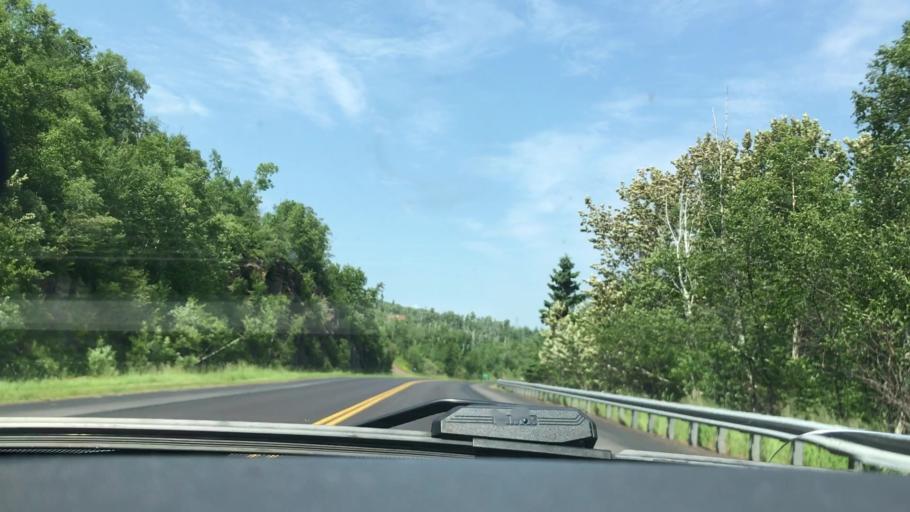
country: US
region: Minnesota
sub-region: Lake County
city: Silver Bay
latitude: 47.3710
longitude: -91.1659
